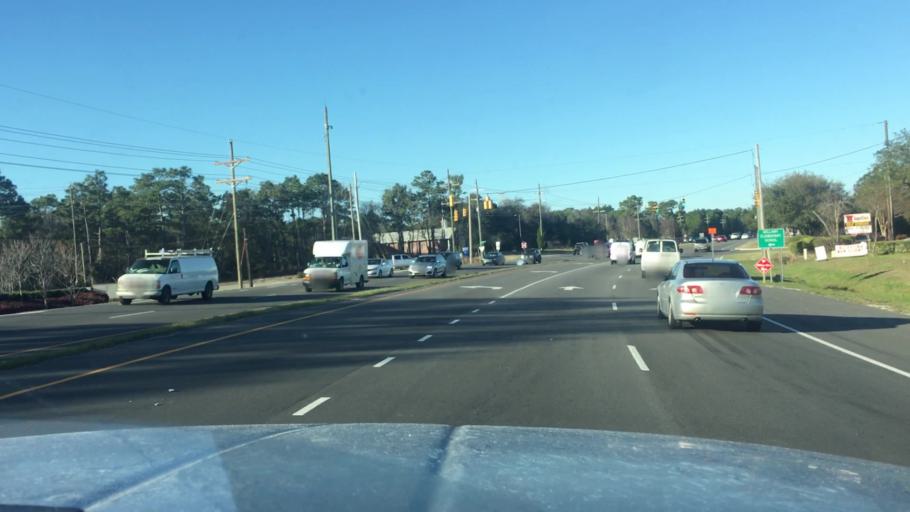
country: US
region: North Carolina
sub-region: New Hanover County
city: Myrtle Grove
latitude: 34.1251
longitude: -77.8997
